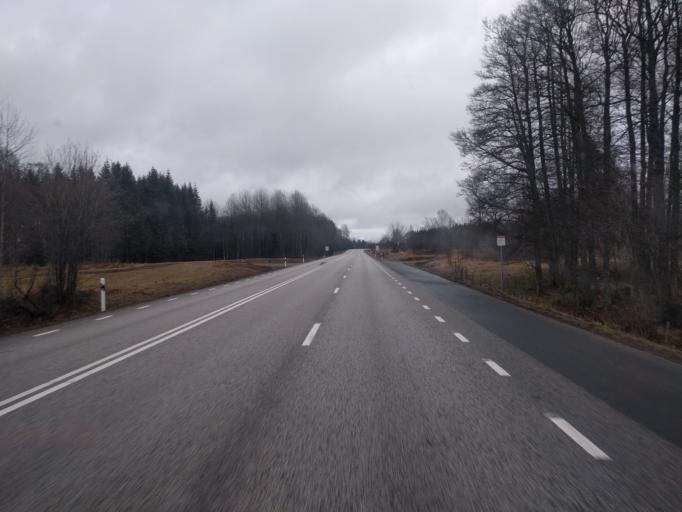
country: SE
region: Joenkoeping
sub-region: Eksjo Kommun
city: Eksjoe
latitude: 57.6385
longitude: 15.0901
